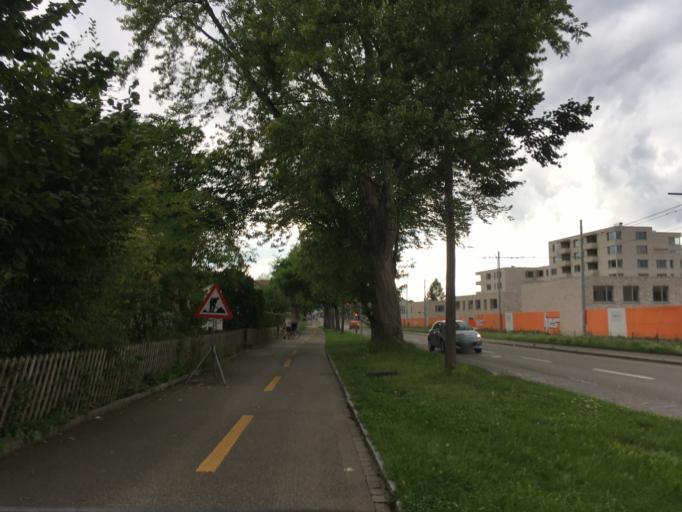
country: CH
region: Zurich
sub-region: Bezirk Zuerich
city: Zuerich (Kreis 12) / Hirzenbach
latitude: 47.3976
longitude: 8.5935
